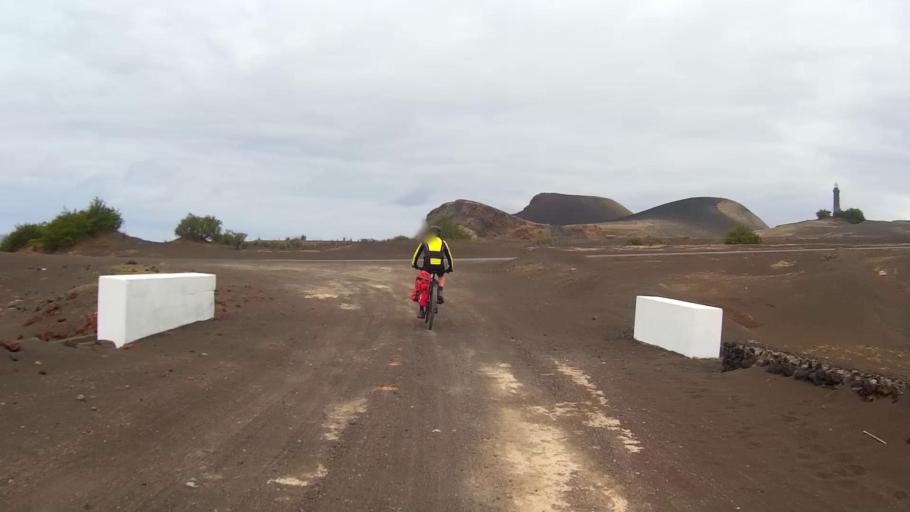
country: PT
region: Azores
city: Ribeira Grande
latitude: 38.5926
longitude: -28.8255
